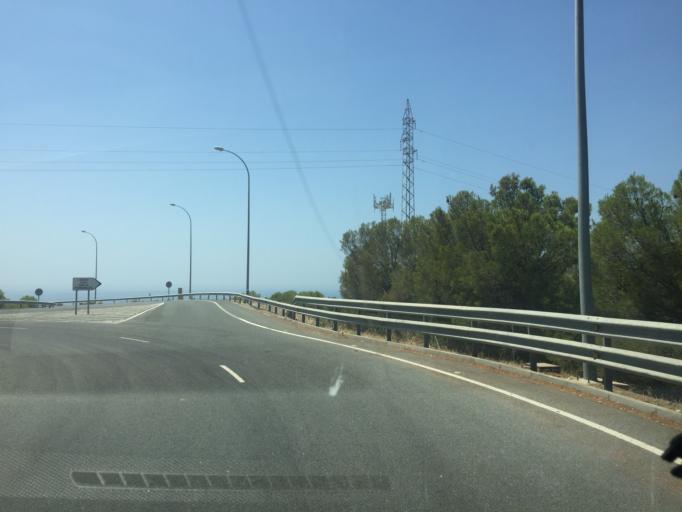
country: ES
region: Andalusia
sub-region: Provincia de Malaga
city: Nerja
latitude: 36.7623
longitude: -3.8544
